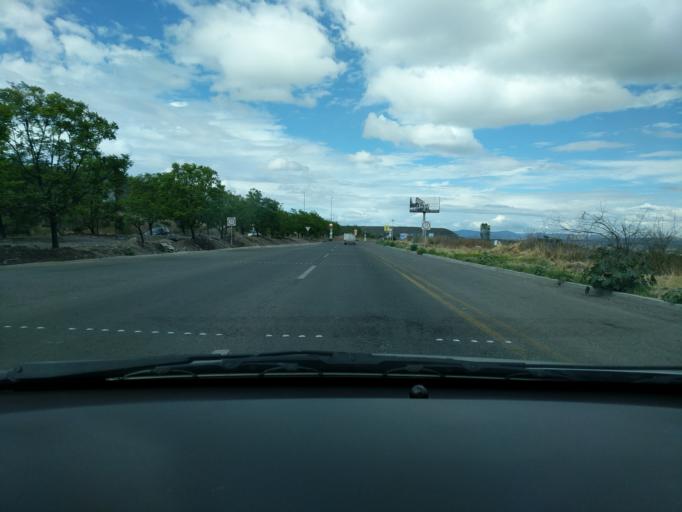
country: MX
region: Queretaro
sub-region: El Marques
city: La Pradera
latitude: 20.6678
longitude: -100.3216
